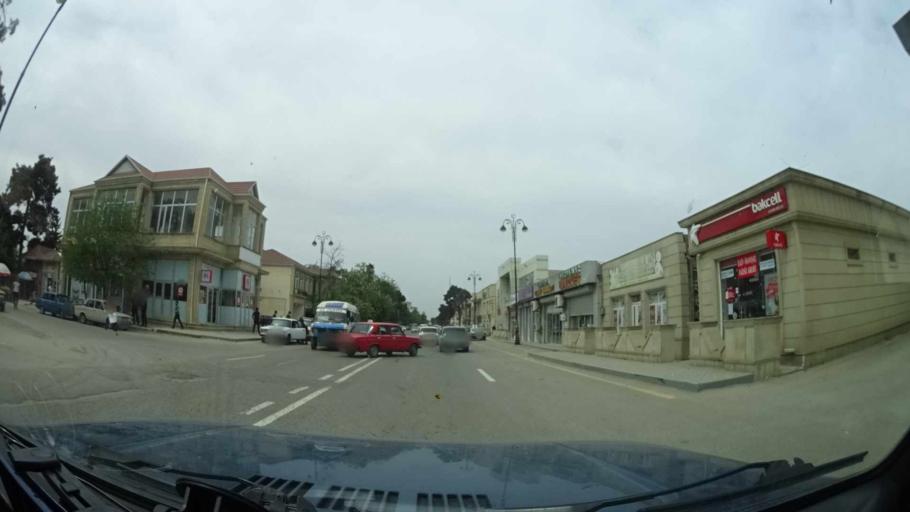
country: AZ
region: Bilasuvar Rayon
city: Pushkino
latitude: 39.4535
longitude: 48.5476
